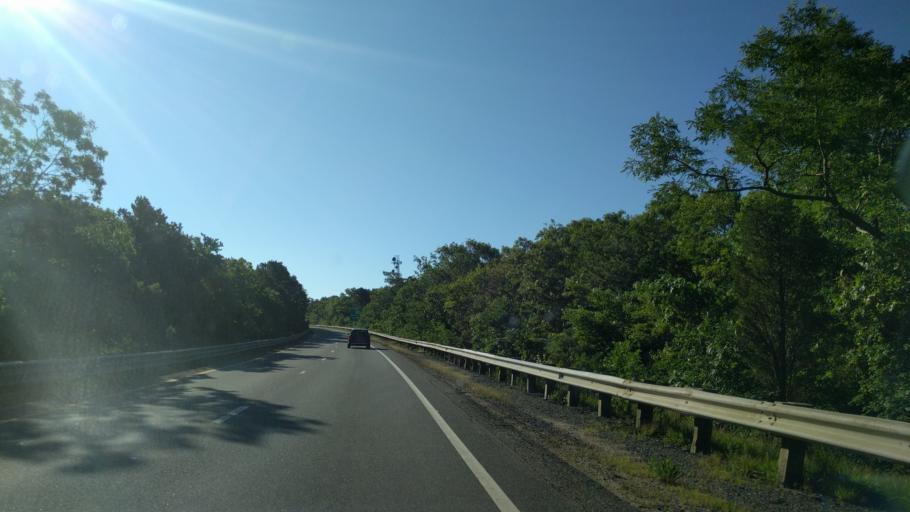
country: US
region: Massachusetts
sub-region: Barnstable County
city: West Barnstable
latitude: 41.6858
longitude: -70.3644
